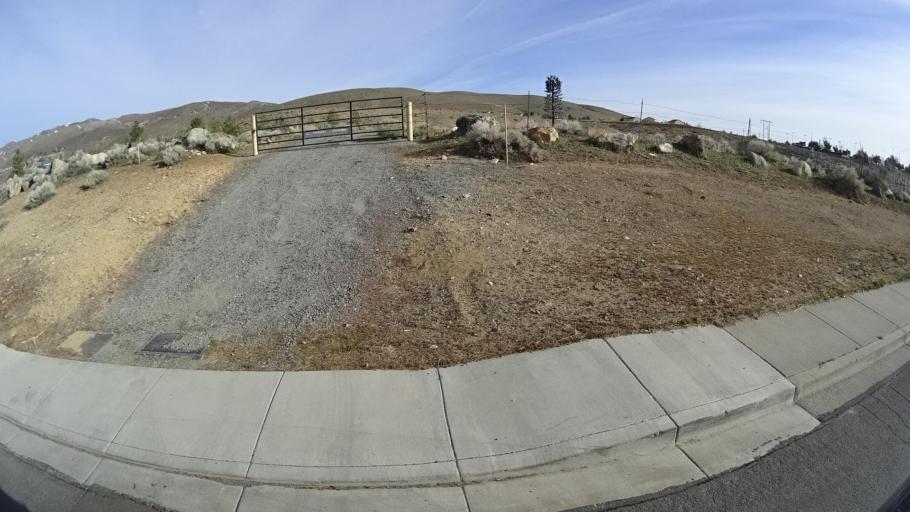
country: US
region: Nevada
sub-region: Washoe County
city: Reno
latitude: 39.5410
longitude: -119.8671
